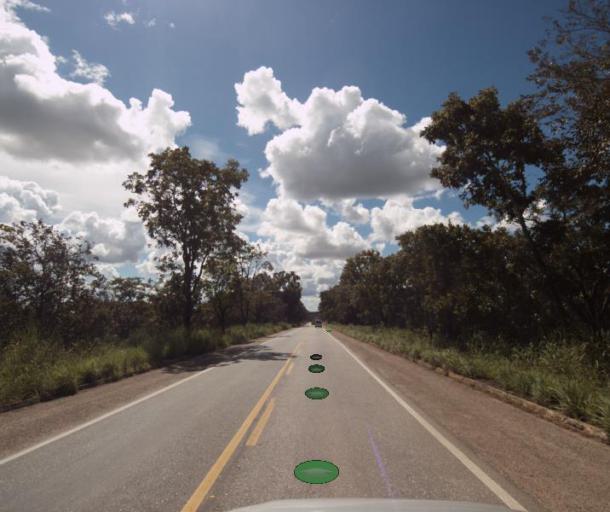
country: BR
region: Goias
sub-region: Porangatu
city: Porangatu
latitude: -13.6607
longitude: -49.0336
